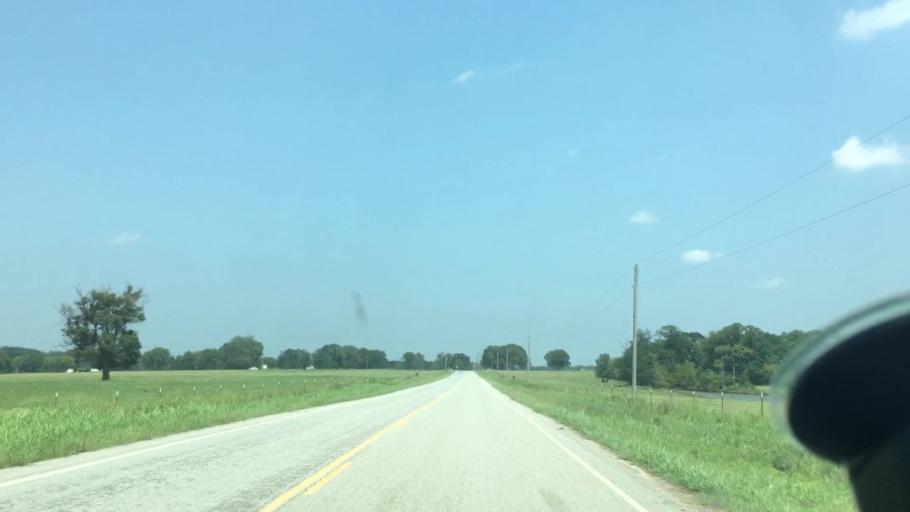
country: US
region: Oklahoma
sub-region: Atoka County
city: Atoka
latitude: 34.2733
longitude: -95.9361
